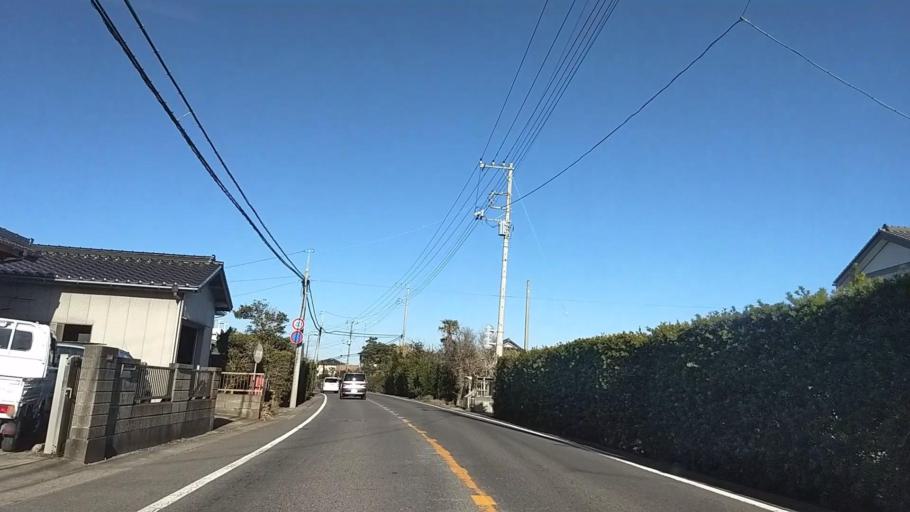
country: JP
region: Chiba
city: Naruto
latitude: 35.5730
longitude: 140.4846
